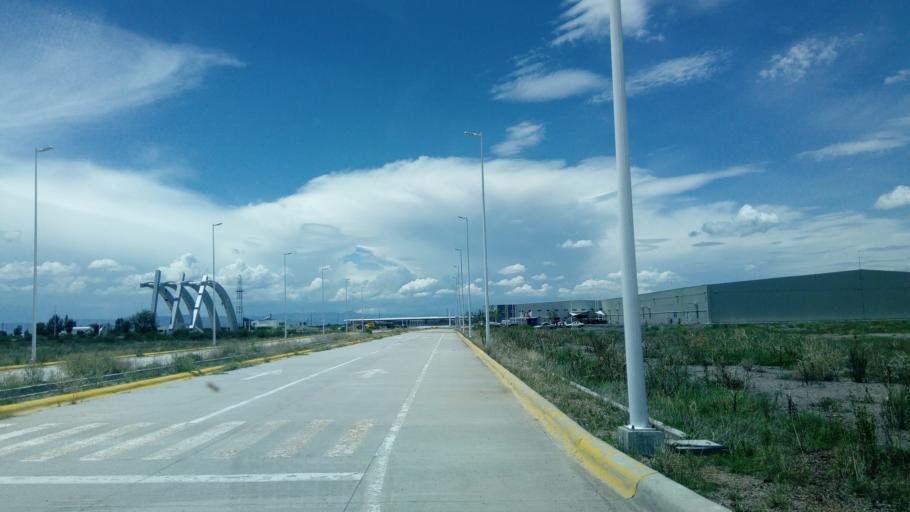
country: MX
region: Durango
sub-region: Durango
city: Jose Refugio Salcido
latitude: 24.1592
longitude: -104.5132
